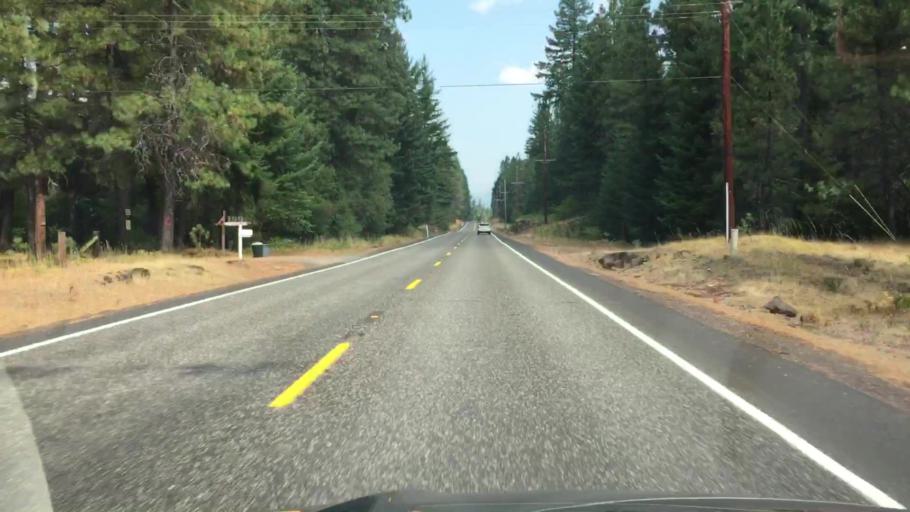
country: US
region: Washington
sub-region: Klickitat County
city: White Salmon
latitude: 45.9344
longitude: -121.4939
